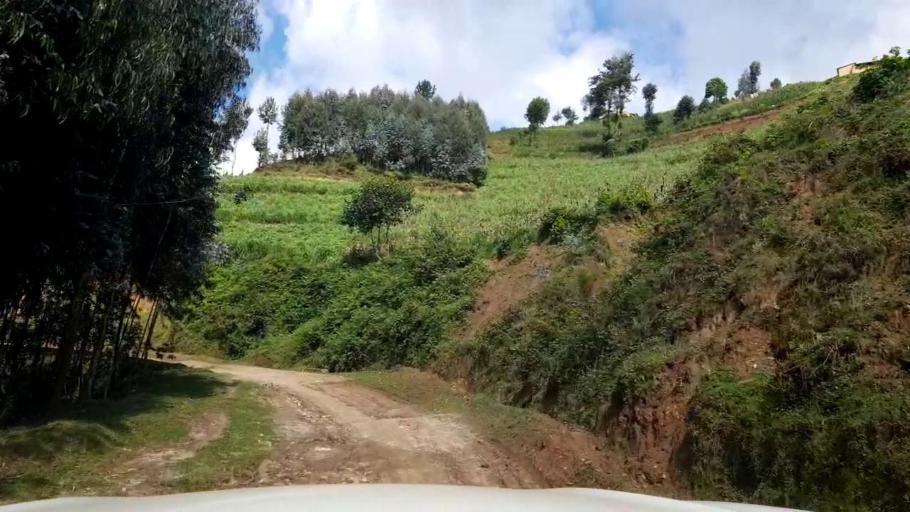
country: RW
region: Western Province
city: Kibuye
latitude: -1.8824
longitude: 29.4683
